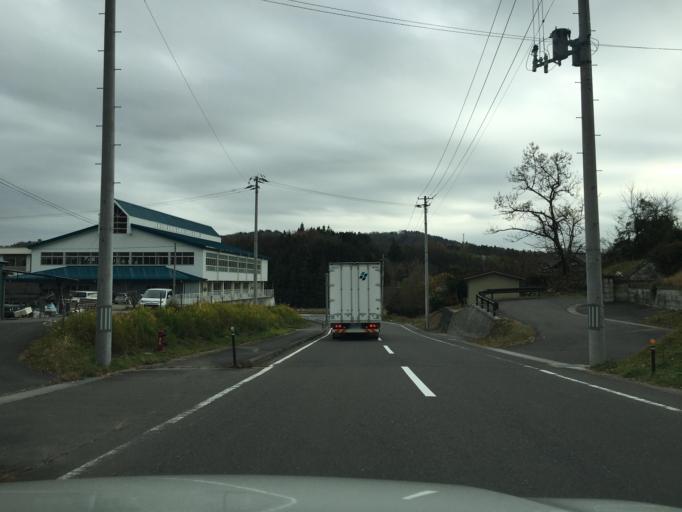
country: JP
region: Fukushima
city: Miharu
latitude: 37.5034
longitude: 140.4728
